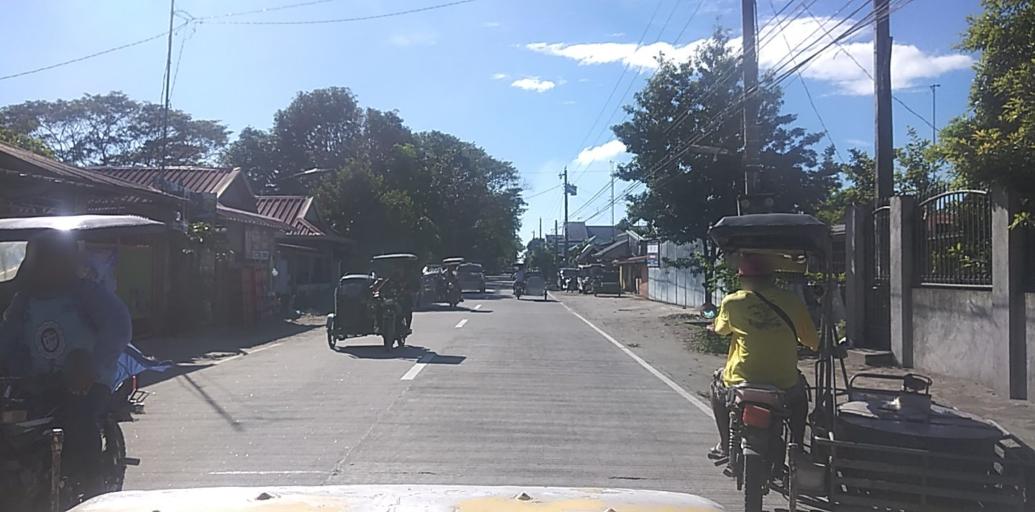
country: PH
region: Central Luzon
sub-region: Province of Pampanga
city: San Patricio
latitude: 15.0893
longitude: 120.7136
